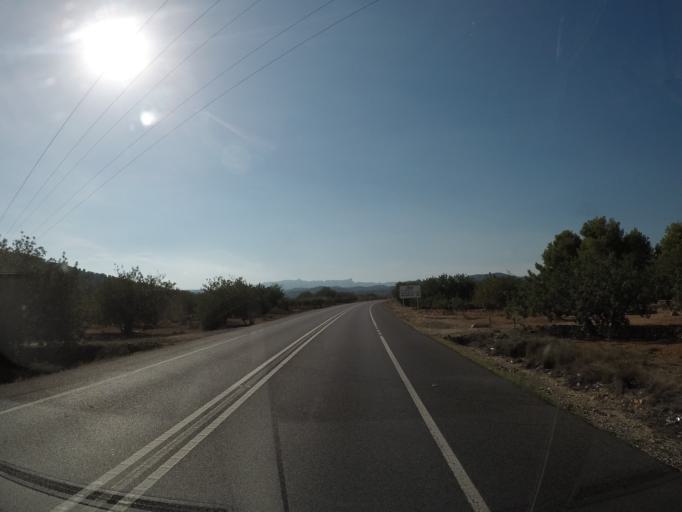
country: ES
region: Catalonia
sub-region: Provincia de Tarragona
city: El Perello
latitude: 40.8968
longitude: 0.7442
